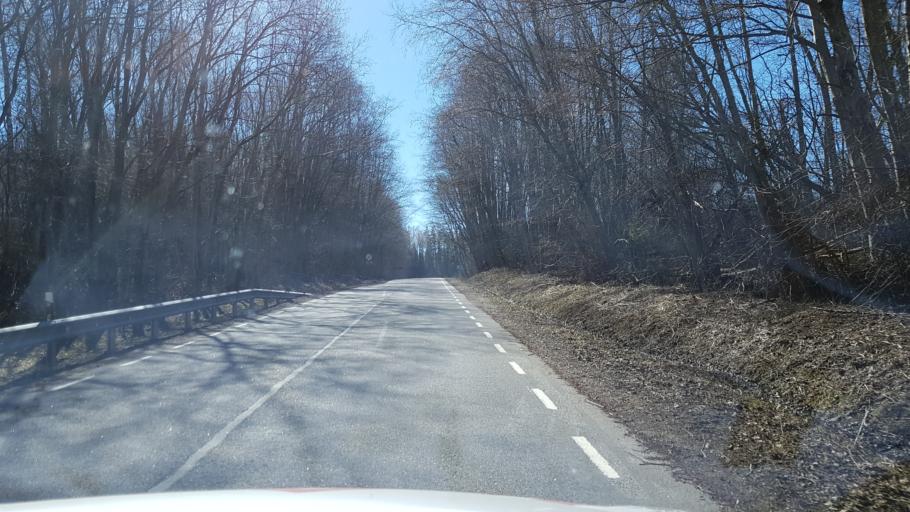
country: EE
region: Laeaene-Virumaa
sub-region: Viru-Nigula vald
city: Kunda
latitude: 59.5205
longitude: 26.4698
